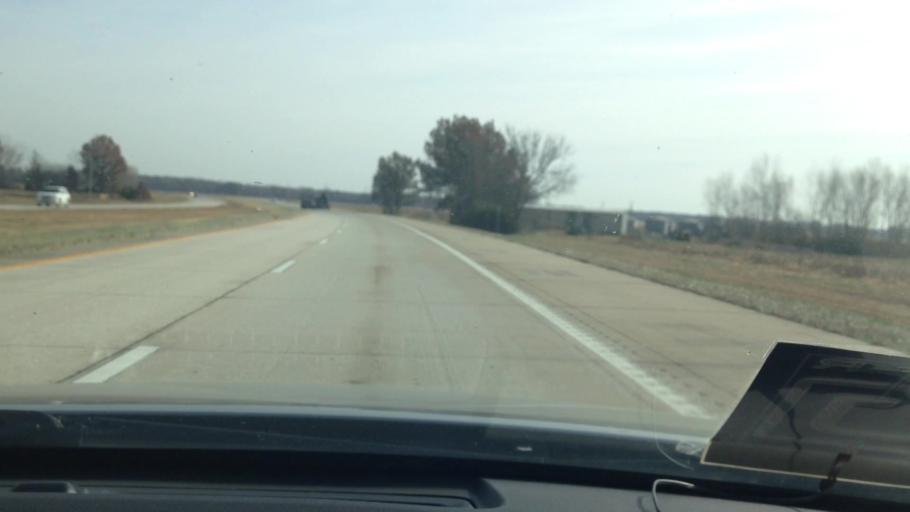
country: US
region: Missouri
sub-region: Henry County
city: Clinton
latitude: 38.4300
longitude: -93.9240
